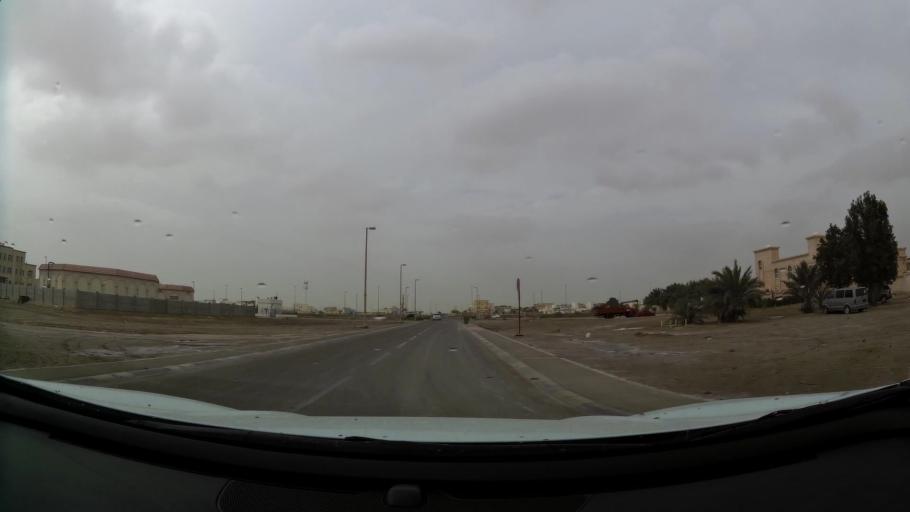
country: AE
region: Abu Dhabi
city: Abu Dhabi
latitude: 24.3585
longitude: 54.6604
